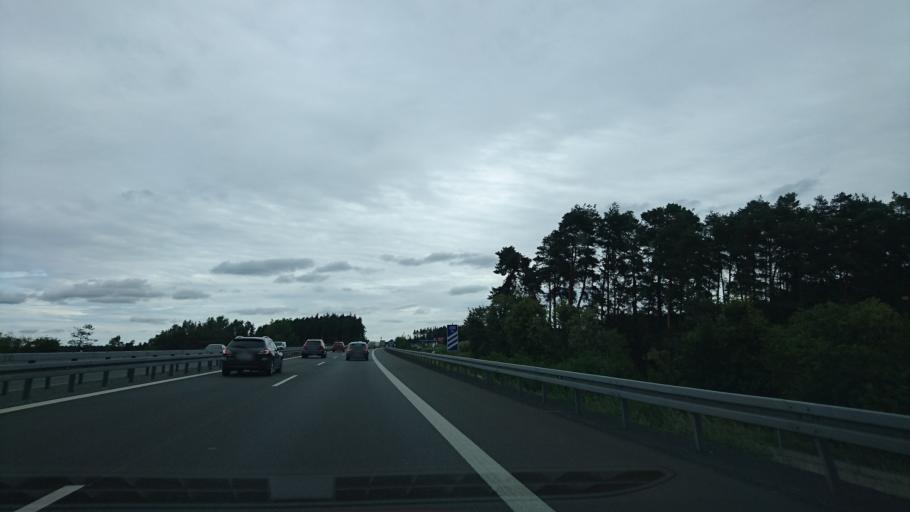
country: DE
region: Bavaria
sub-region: Upper Palatinate
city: Berg
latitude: 49.8311
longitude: 12.1670
